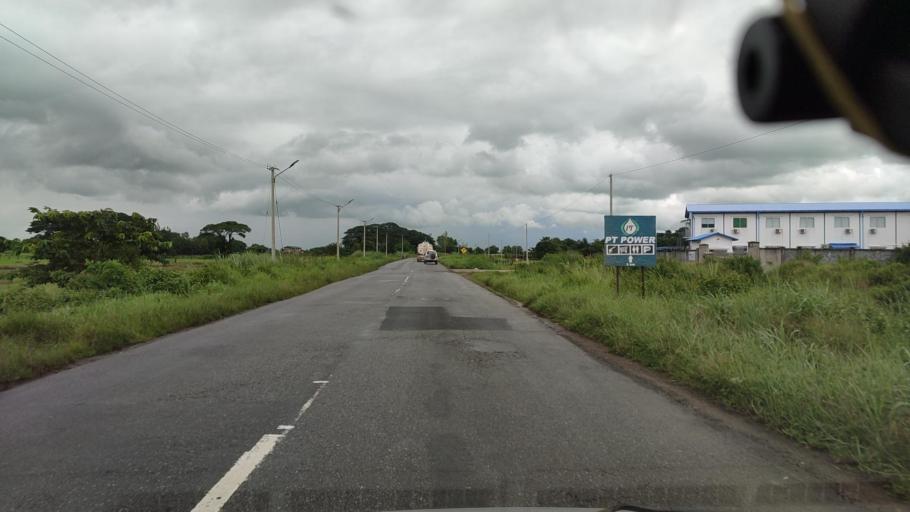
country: MM
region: Bago
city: Bago
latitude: 17.3875
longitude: 96.5059
